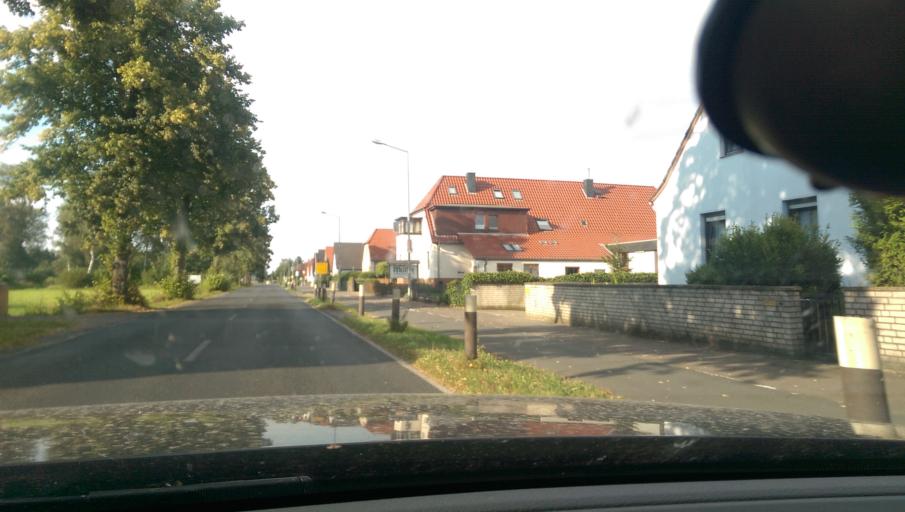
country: DE
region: Lower Saxony
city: Neustadt am Rubenberge
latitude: 52.4836
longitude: 9.4562
